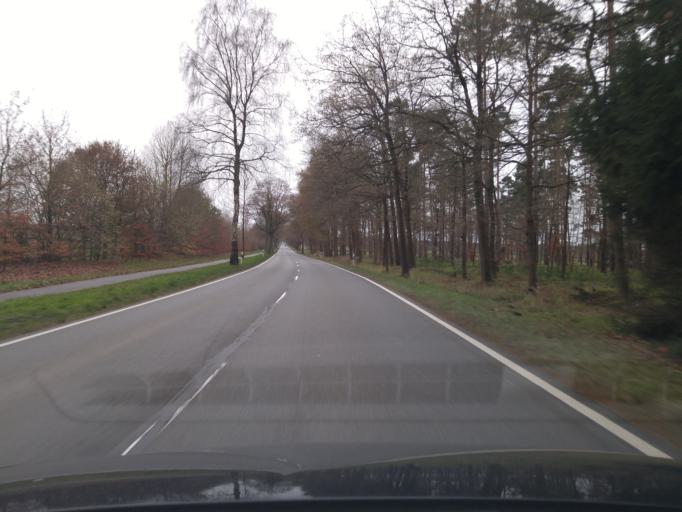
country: DE
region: Lower Saxony
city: Winsen
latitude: 52.7073
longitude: 9.9166
